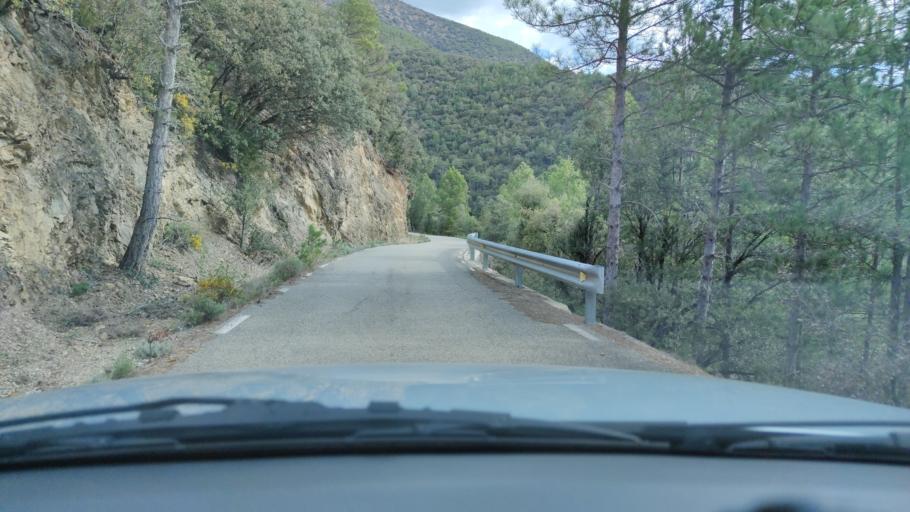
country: ES
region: Catalonia
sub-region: Provincia de Lleida
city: la Seu d'Urgell
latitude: 42.2412
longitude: 1.4289
